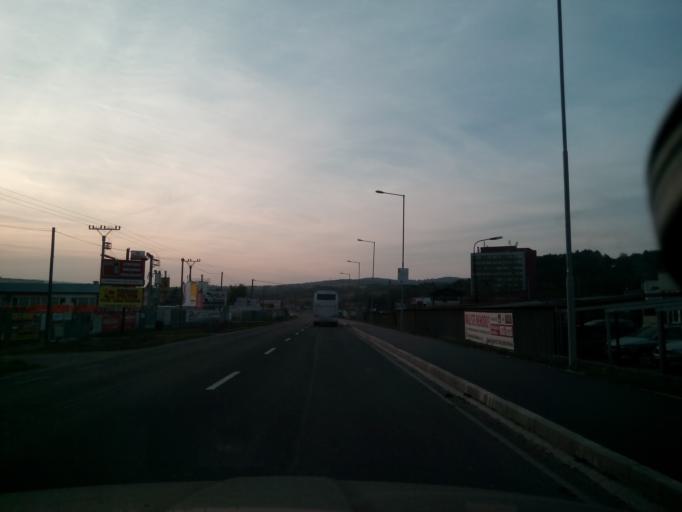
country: SK
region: Presovsky
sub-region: Okres Bardejov
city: Bardejov
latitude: 49.3053
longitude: 21.2981
